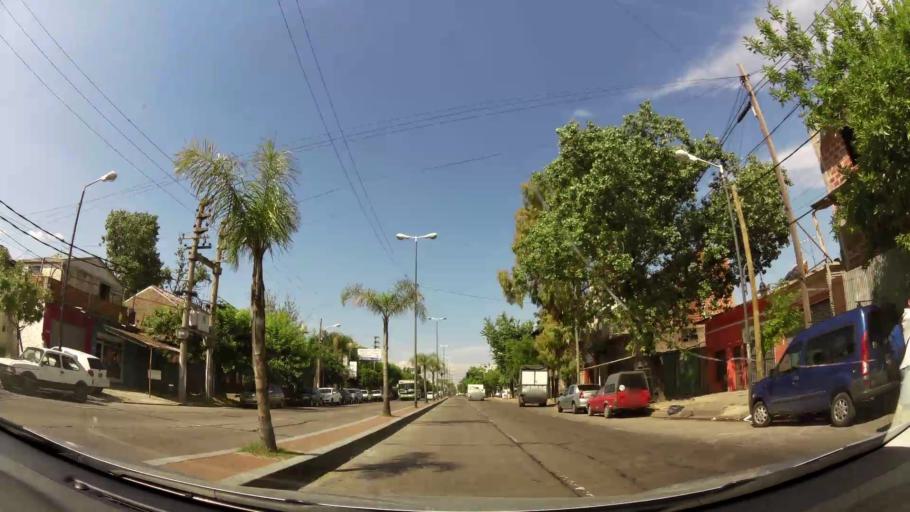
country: AR
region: Buenos Aires
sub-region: Partido de Tigre
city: Tigre
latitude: -34.4699
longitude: -58.5919
